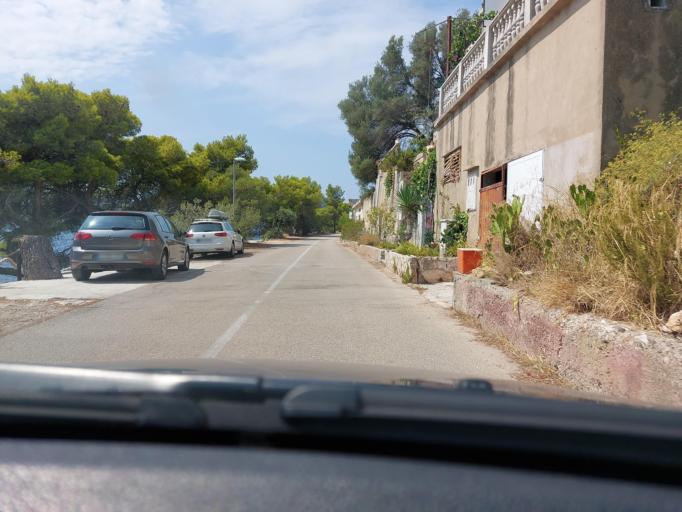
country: HR
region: Dubrovacko-Neretvanska
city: Smokvica
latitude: 42.7504
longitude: 16.8266
